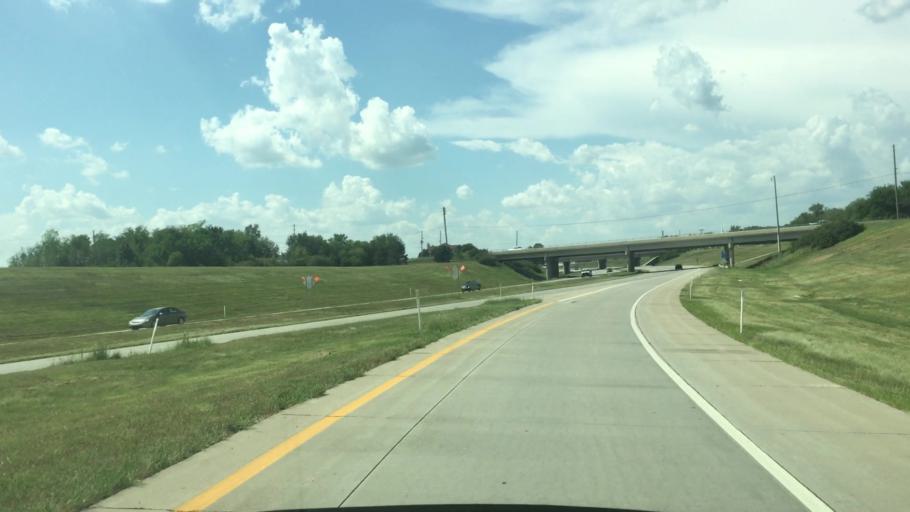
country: US
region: Kansas
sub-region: Butler County
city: Andover
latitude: 37.6923
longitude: -97.1862
